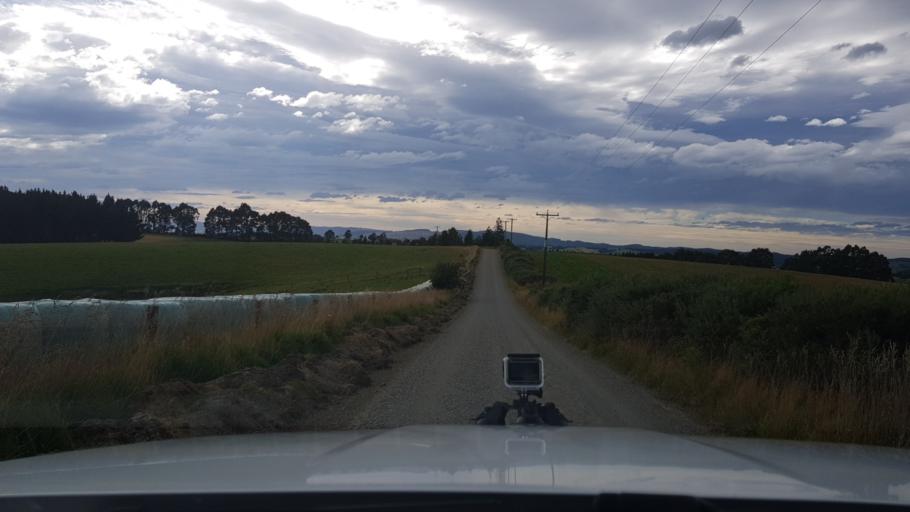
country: NZ
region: Otago
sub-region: Clutha District
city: Balclutha
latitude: -46.2007
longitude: 169.7546
